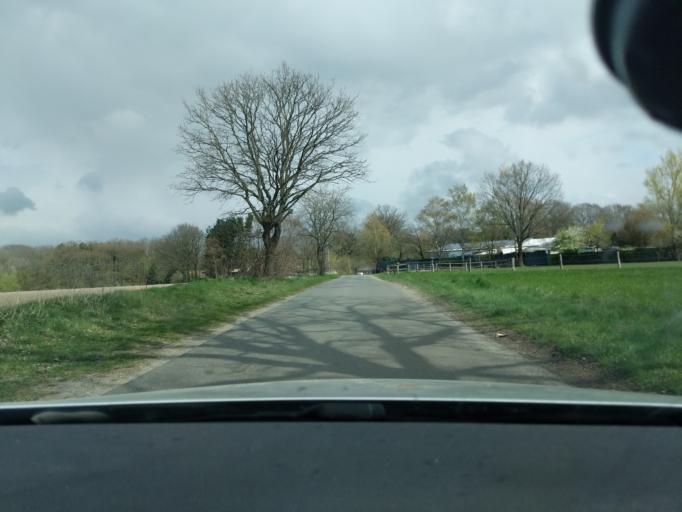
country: DE
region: Lower Saxony
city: Stade
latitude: 53.5731
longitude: 9.4668
